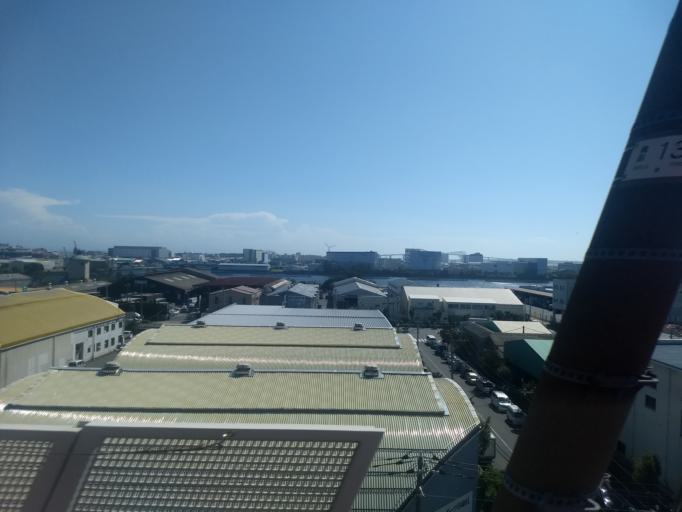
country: JP
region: Tokyo
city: Urayasu
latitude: 35.6463
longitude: 139.8303
